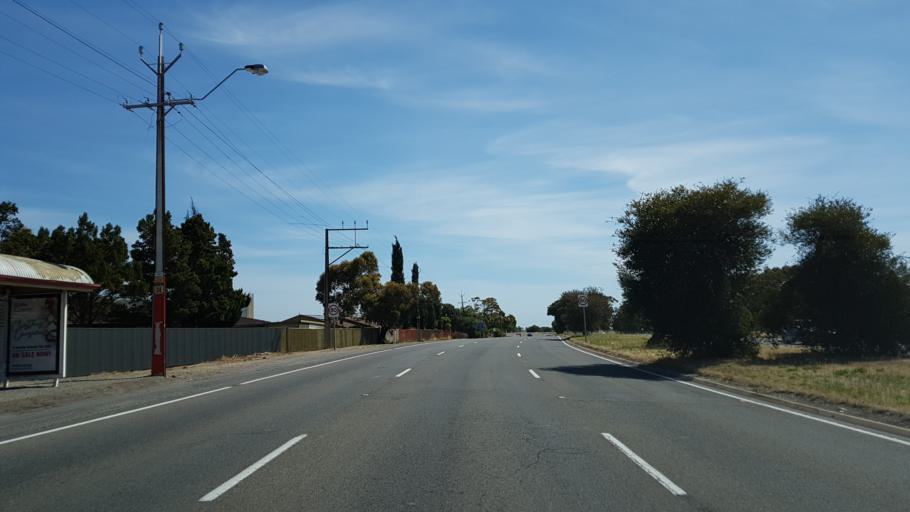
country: AU
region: South Australia
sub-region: Marion
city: Trott Park
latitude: -35.0615
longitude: 138.5587
